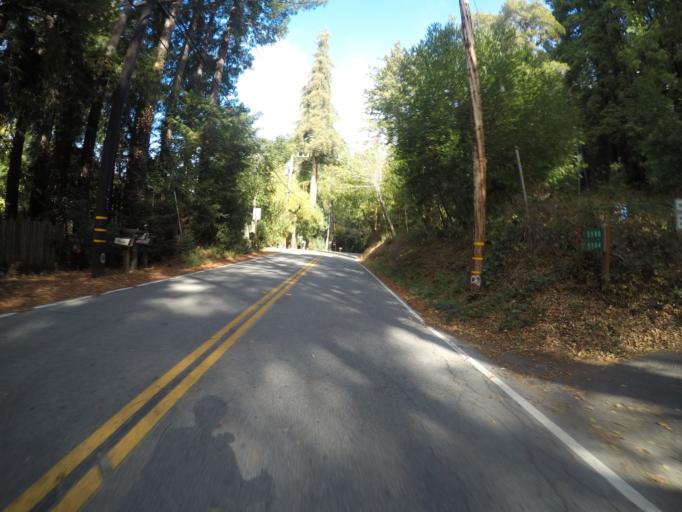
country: US
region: California
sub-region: Santa Cruz County
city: Scotts Valley
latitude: 37.0530
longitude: -121.9782
